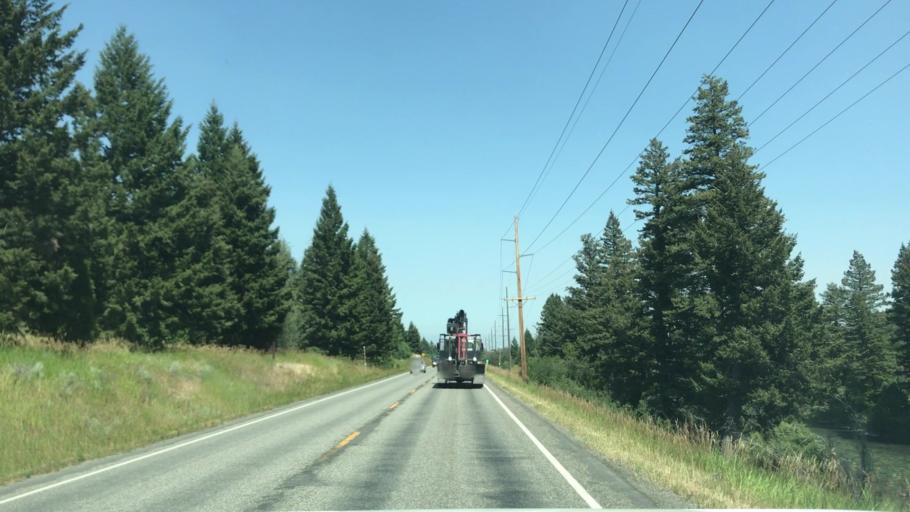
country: US
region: Montana
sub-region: Gallatin County
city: Four Corners
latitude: 45.5155
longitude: -111.2560
